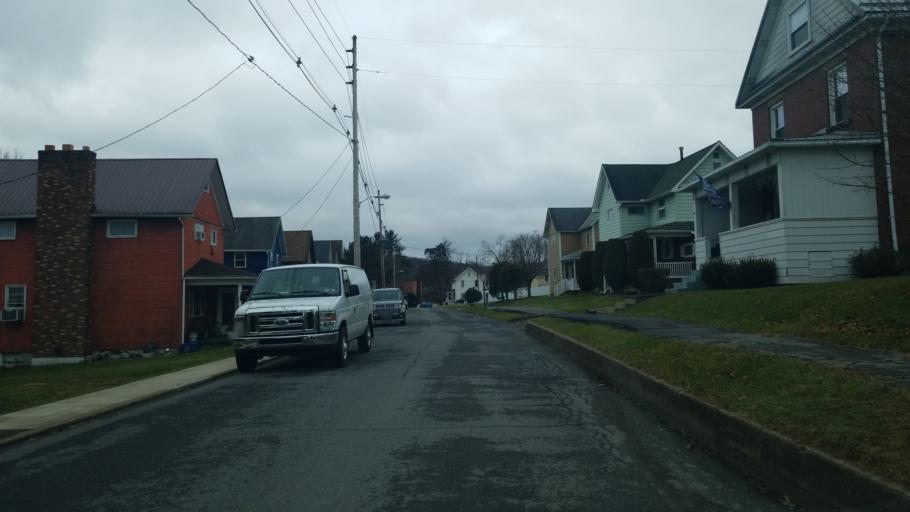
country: US
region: Pennsylvania
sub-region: Clearfield County
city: Sandy
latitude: 41.1140
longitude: -78.7716
